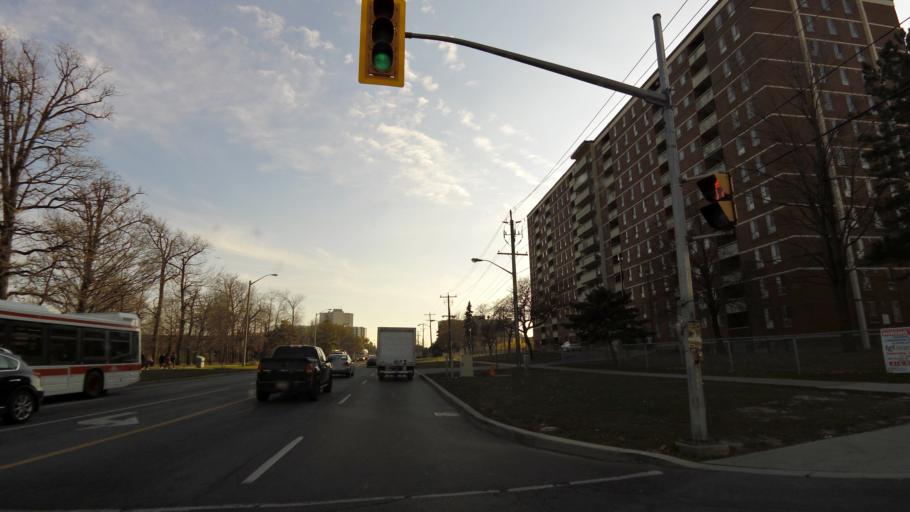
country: CA
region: Ontario
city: Concord
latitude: 43.7659
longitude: -79.5197
